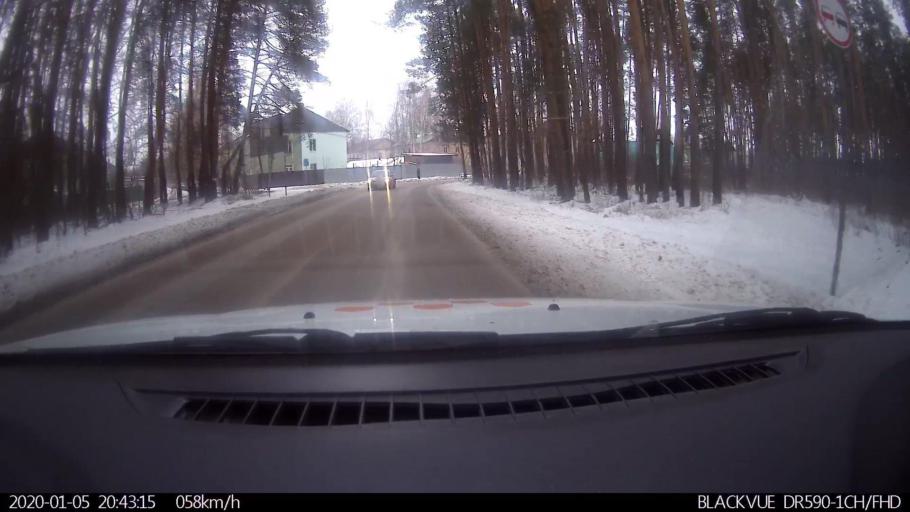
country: RU
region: Nizjnij Novgorod
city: Lukino
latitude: 56.3915
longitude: 43.7390
